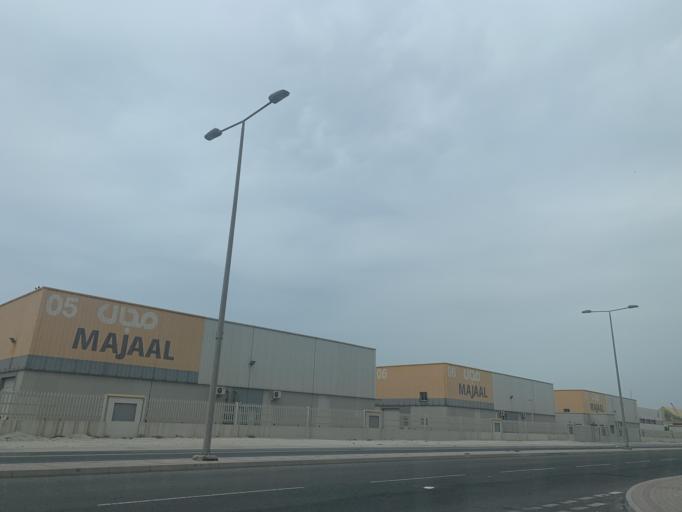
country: BH
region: Muharraq
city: Al Hadd
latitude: 26.2147
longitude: 50.6742
